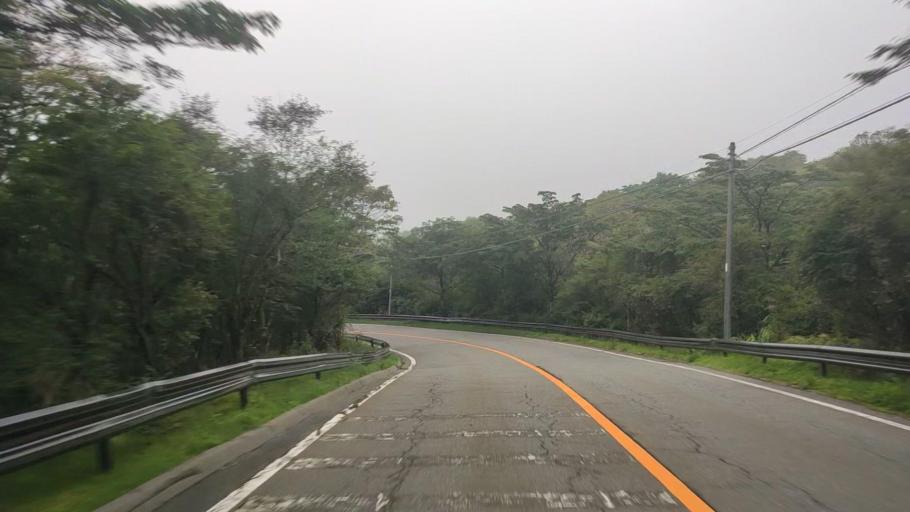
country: JP
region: Shizuoka
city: Fuji
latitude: 35.2954
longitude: 138.7675
